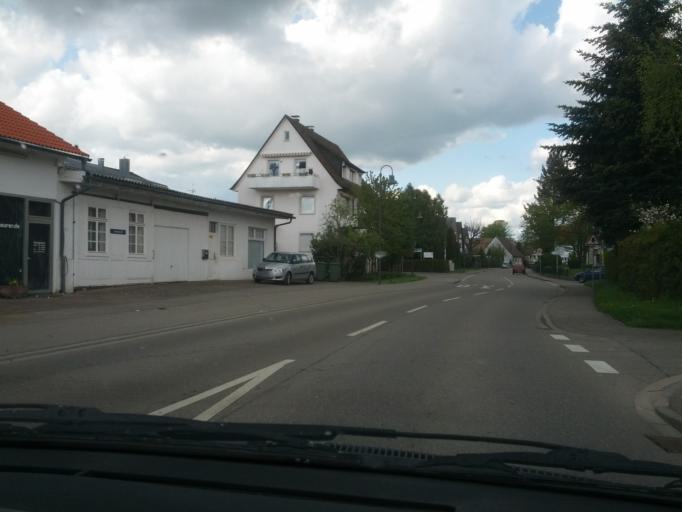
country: DE
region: Baden-Wuerttemberg
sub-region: Freiburg Region
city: Denzlingen
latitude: 48.0678
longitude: 7.8698
